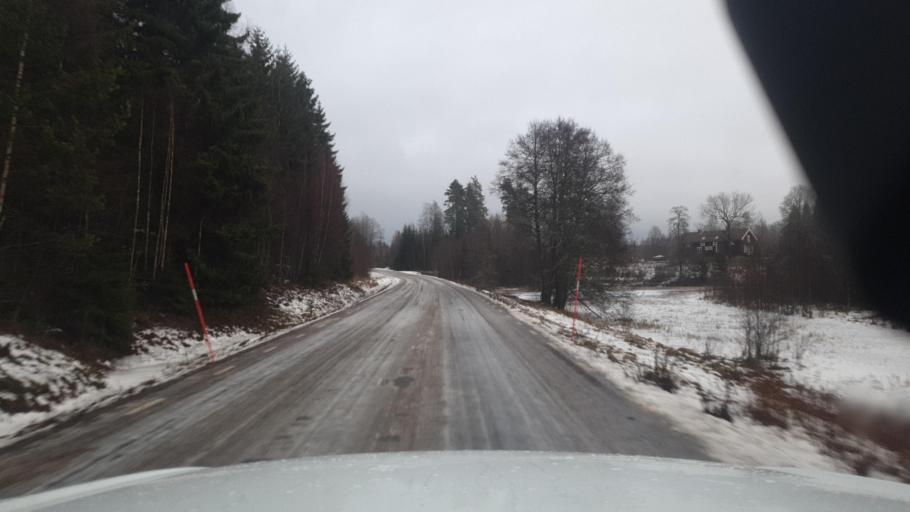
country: SE
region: Vaermland
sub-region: Torsby Kommun
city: Torsby
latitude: 59.9817
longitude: 12.8210
